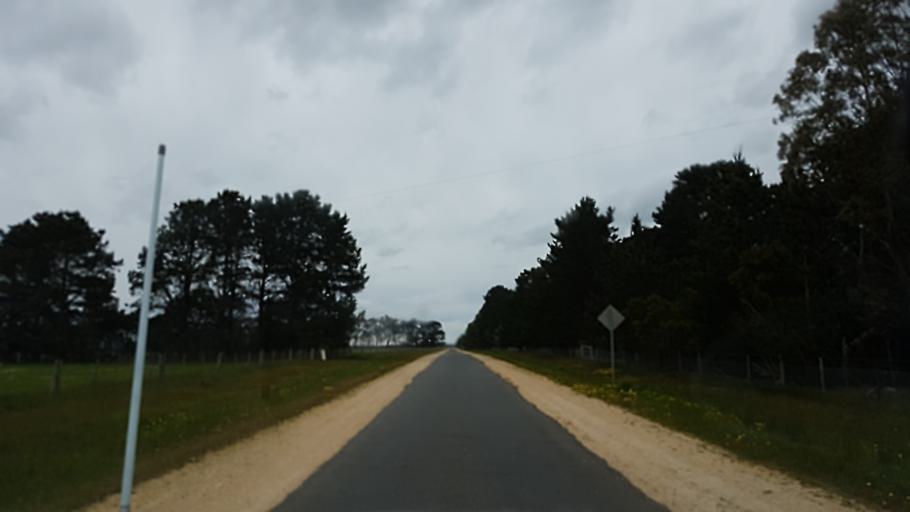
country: AU
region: Victoria
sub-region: Moorabool
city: Bacchus Marsh
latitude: -37.7536
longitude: 144.1552
